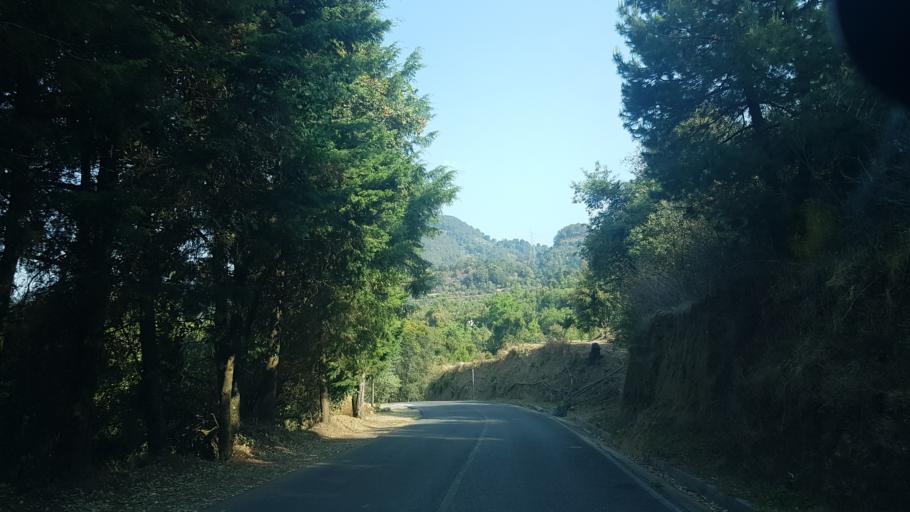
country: MX
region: Puebla
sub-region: Tochimilco
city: Santa Cruz Cuautomatitla
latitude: 18.8930
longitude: -98.6721
